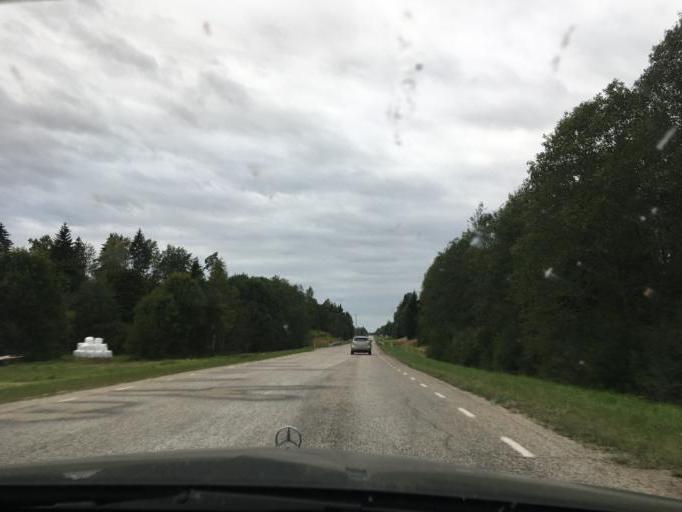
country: LV
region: Aluksnes Rajons
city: Aluksne
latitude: 57.5852
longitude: 27.0677
